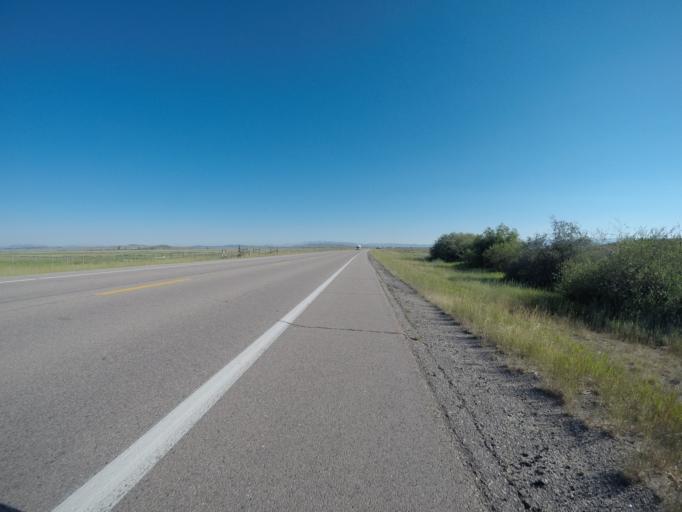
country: US
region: Wyoming
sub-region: Sublette County
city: Pinedale
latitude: 42.9523
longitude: -110.0863
